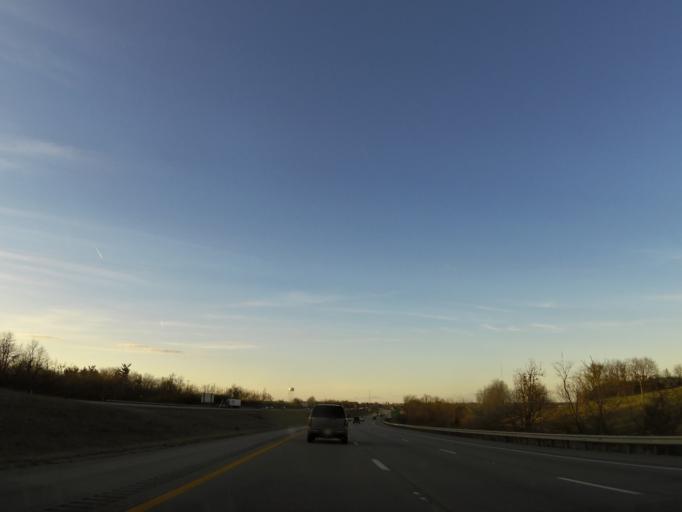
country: US
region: Kentucky
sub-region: Madison County
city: Richmond
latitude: 37.8514
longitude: -84.3312
